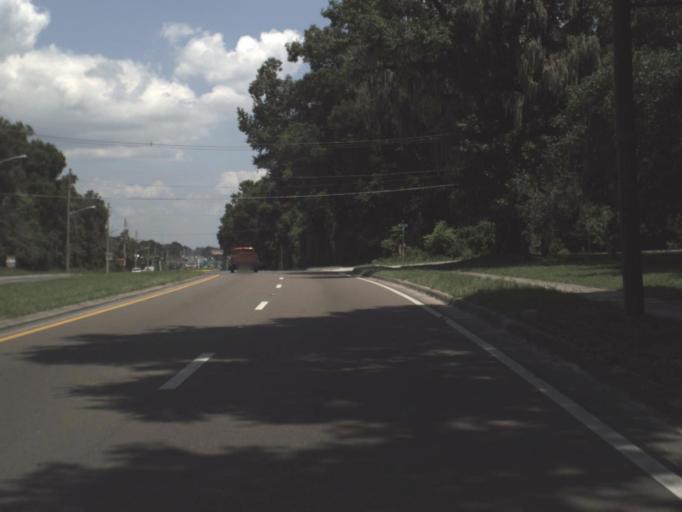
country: US
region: Florida
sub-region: Alachua County
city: Alachua
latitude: 29.6597
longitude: -82.4285
